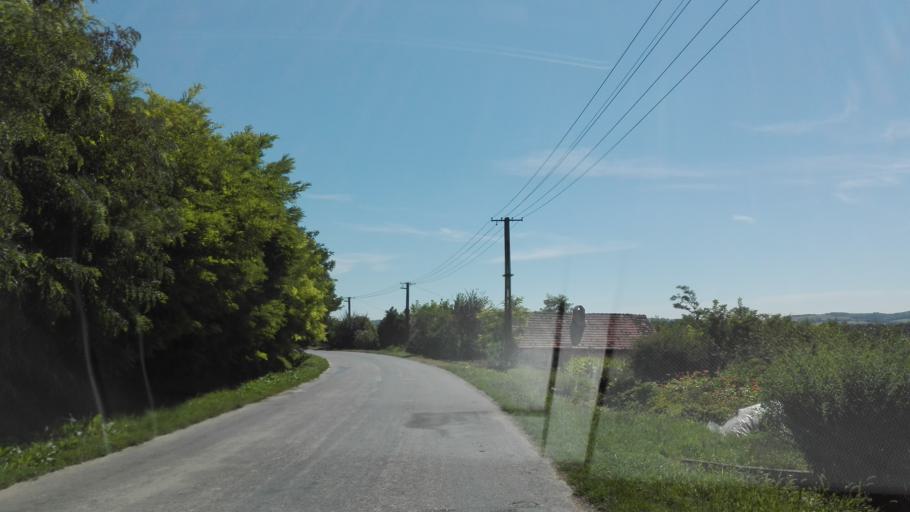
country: HU
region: Tolna
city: Ozora
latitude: 46.7488
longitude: 18.4510
